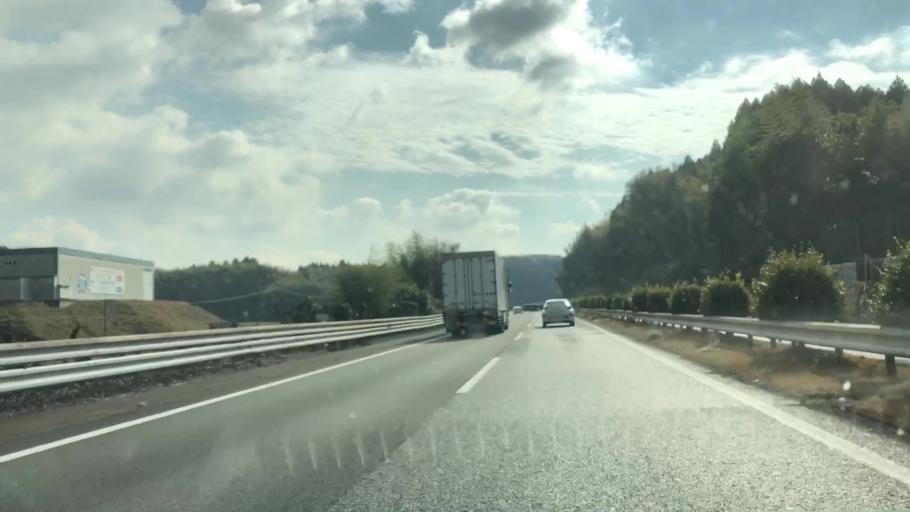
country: JP
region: Fukuoka
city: Setakamachi-takayanagi
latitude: 33.0825
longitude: 130.5416
